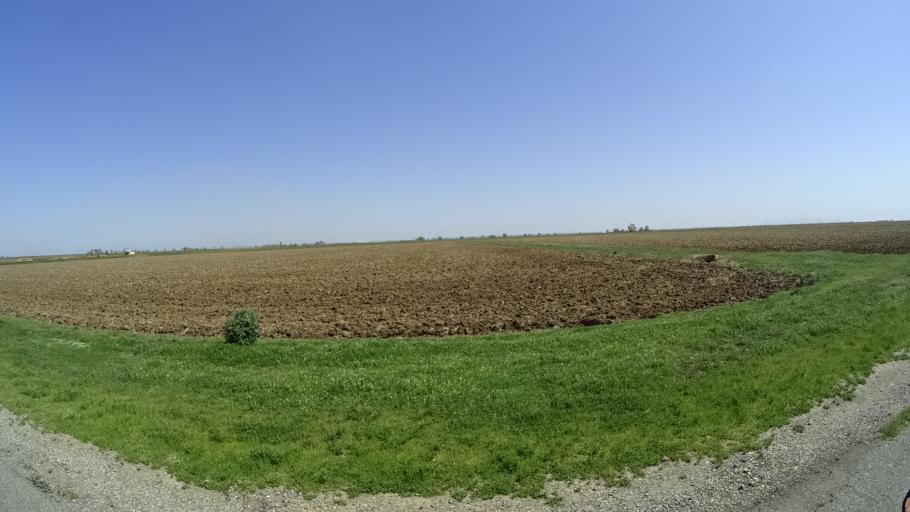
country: US
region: California
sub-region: Glenn County
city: Willows
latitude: 39.4926
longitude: -122.1263
